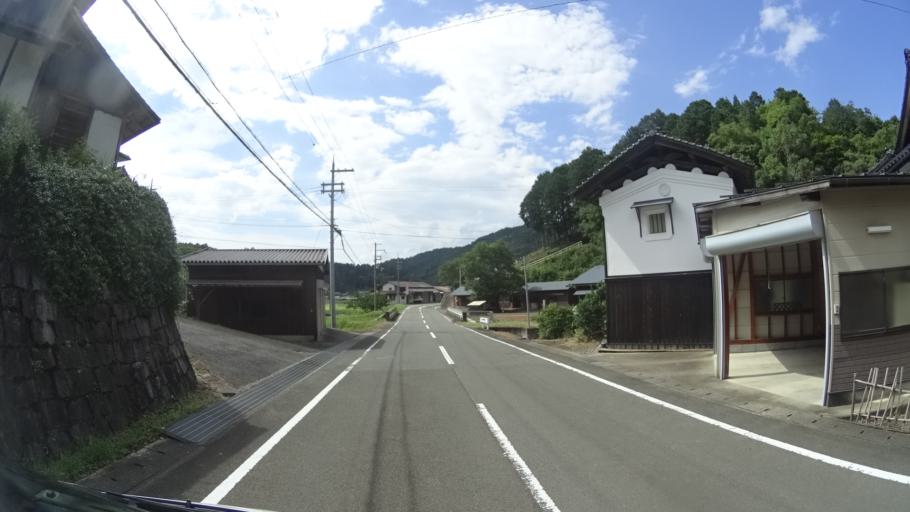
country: JP
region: Kyoto
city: Fukuchiyama
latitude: 35.3714
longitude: 135.1589
